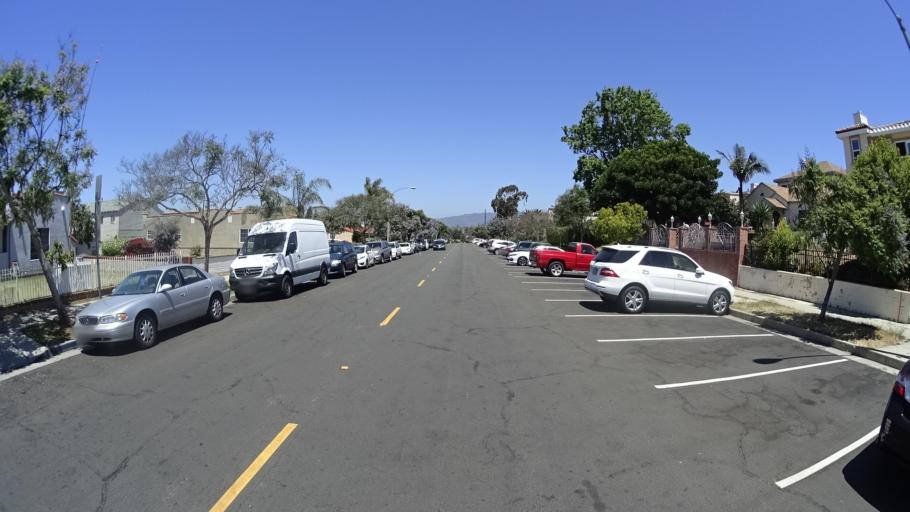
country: US
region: California
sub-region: Los Angeles County
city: Santa Monica
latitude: 34.0153
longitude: -118.4791
